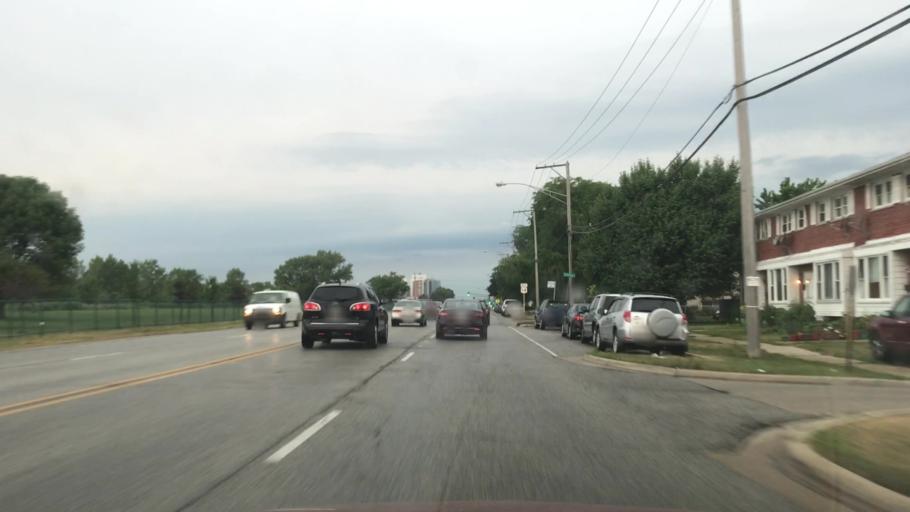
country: US
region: Illinois
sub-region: Cook County
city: Park Ridge
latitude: 42.0402
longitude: -87.8314
